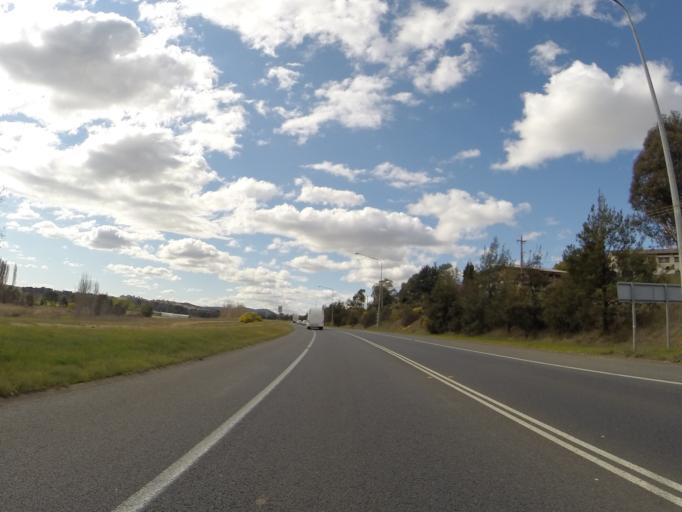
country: AU
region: Australian Capital Territory
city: Belconnen
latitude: -35.2069
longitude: 149.0895
